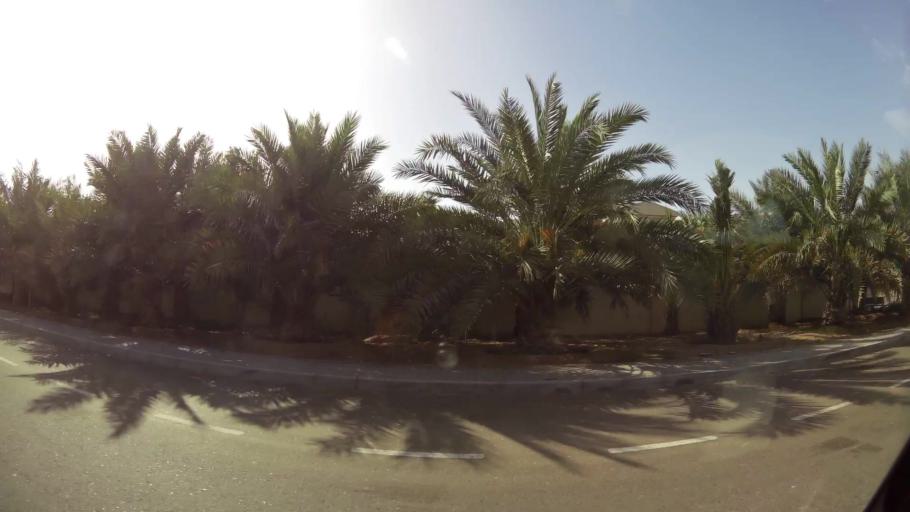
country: OM
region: Al Buraimi
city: Al Buraymi
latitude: 24.3535
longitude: 55.7937
